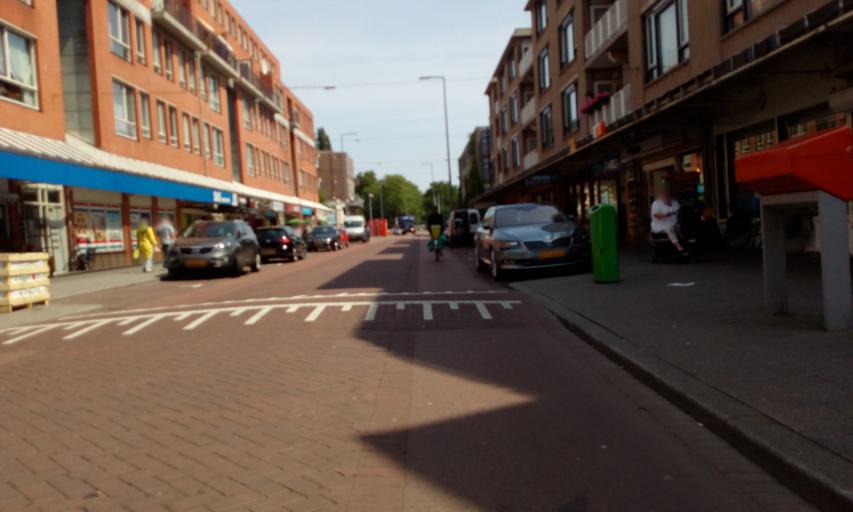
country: NL
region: South Holland
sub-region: Gemeente Rotterdam
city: Rotterdam
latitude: 51.9314
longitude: 4.4932
